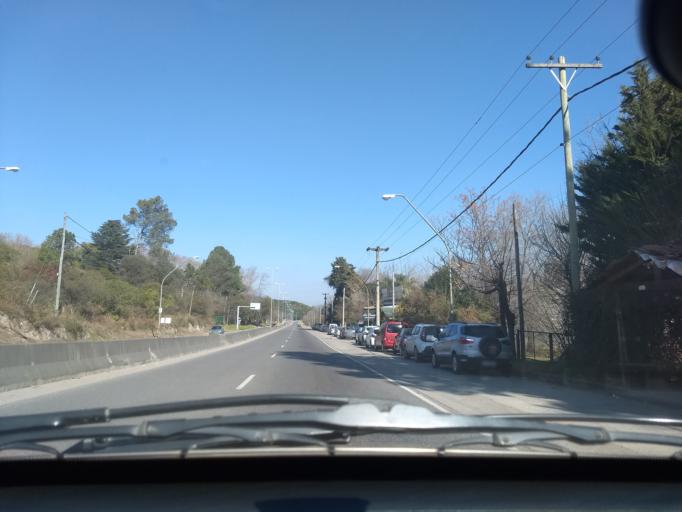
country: AR
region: Cordoba
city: Rio Ceballos
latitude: -31.1612
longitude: -64.3013
